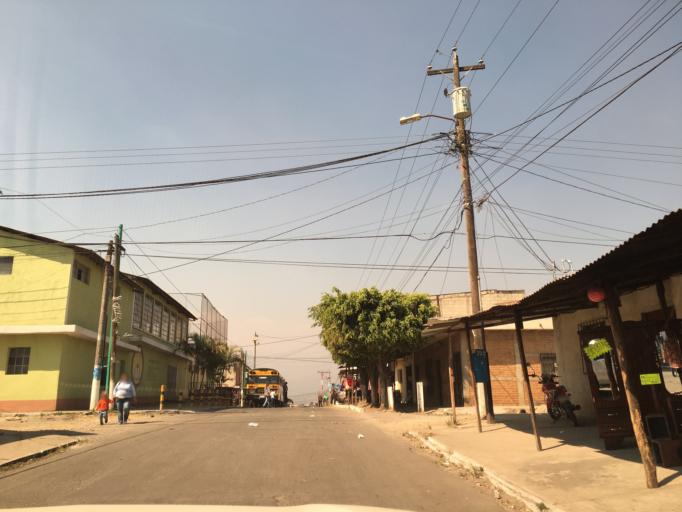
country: GT
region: Guatemala
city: Amatitlan
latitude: 14.5041
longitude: -90.5991
